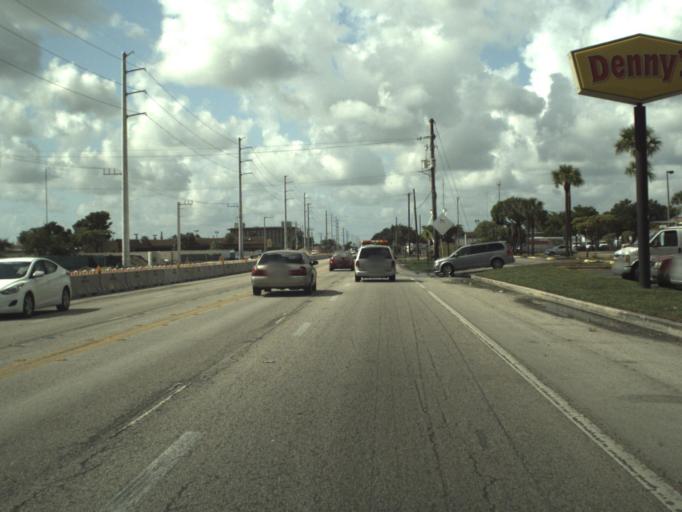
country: US
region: Florida
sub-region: Broward County
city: Pembroke Pines
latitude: 26.0079
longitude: -80.2076
